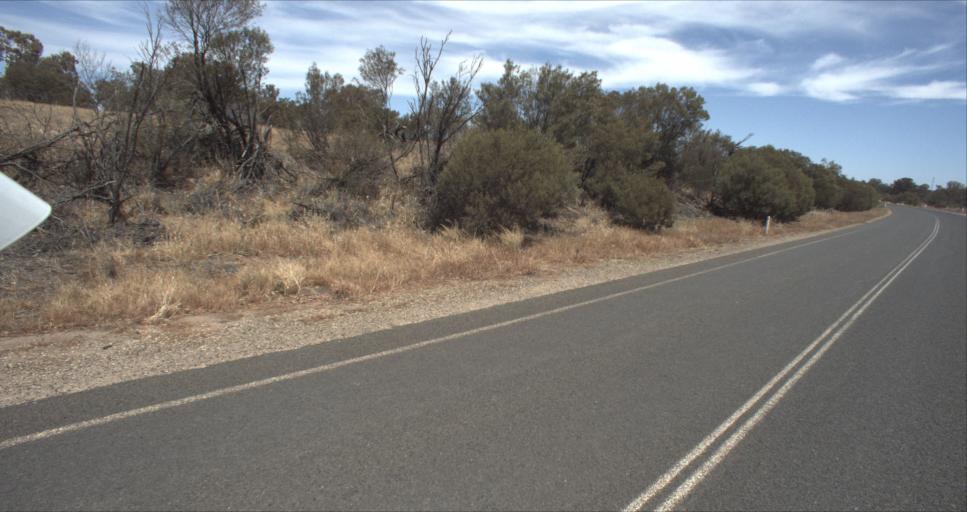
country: AU
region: New South Wales
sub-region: Leeton
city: Leeton
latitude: -34.6599
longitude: 146.4541
